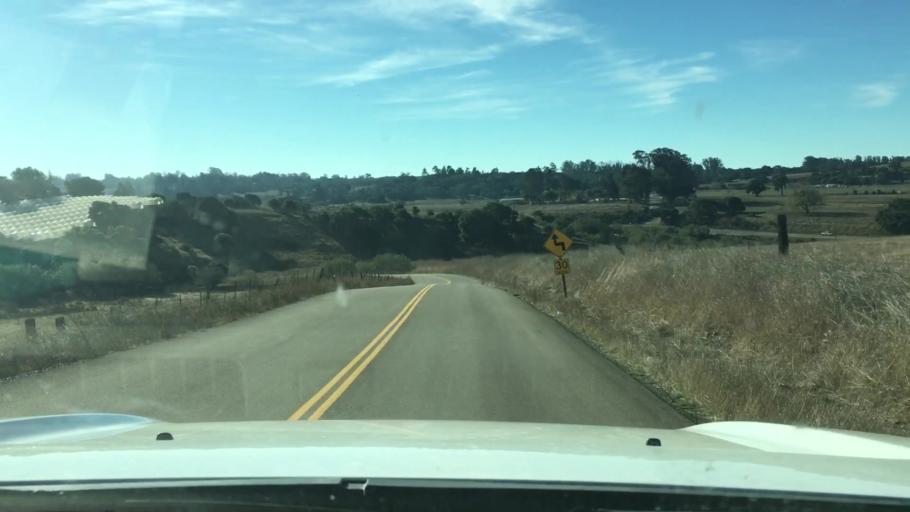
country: US
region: California
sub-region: San Luis Obispo County
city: Arroyo Grande
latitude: 35.0975
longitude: -120.5609
